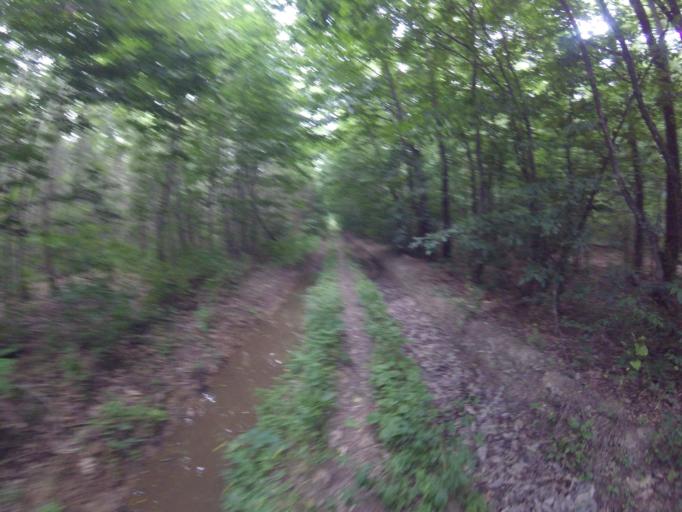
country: HU
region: Zala
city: Turje
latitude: 47.0125
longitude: 17.1485
